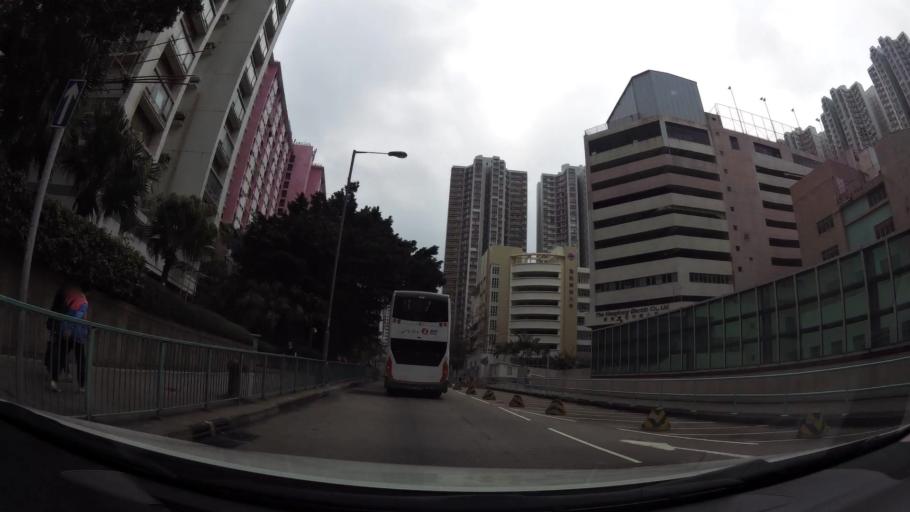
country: HK
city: Yung Shue Wan
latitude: 22.2444
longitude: 114.1477
